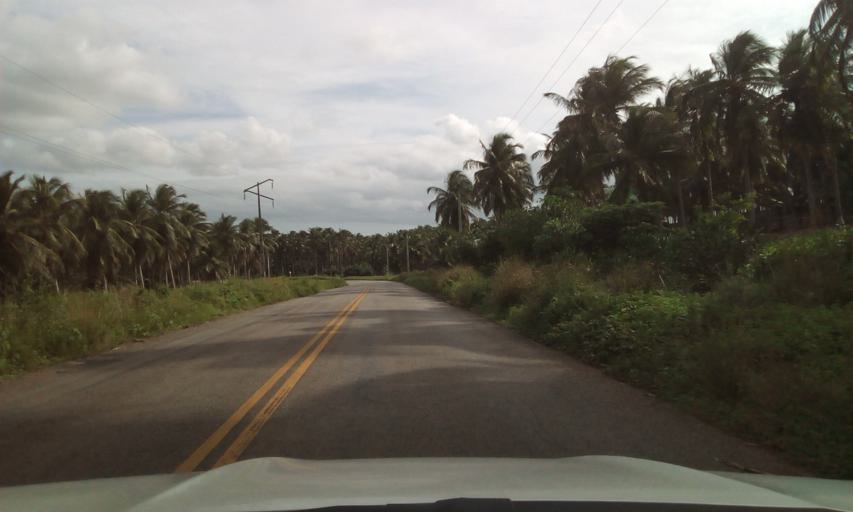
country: BR
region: Paraiba
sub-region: Cabedelo
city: Cabedelo
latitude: -6.9541
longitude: -34.9399
